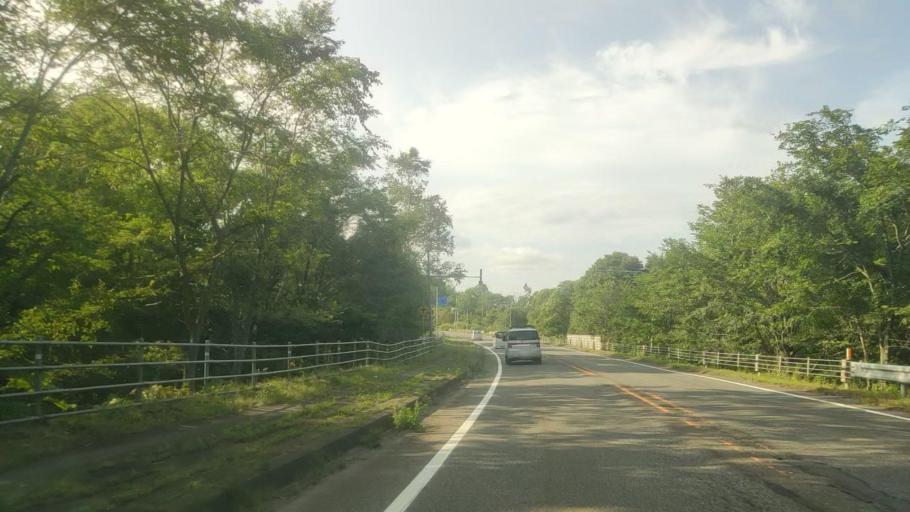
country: JP
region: Hokkaido
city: Chitose
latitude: 42.8733
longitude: 141.8221
